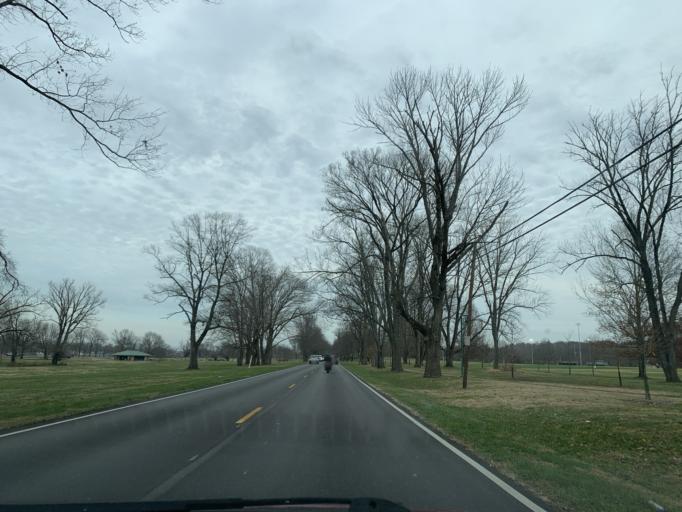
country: US
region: Indiana
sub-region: Clark County
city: Oak Park
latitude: 38.2841
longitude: -85.6898
